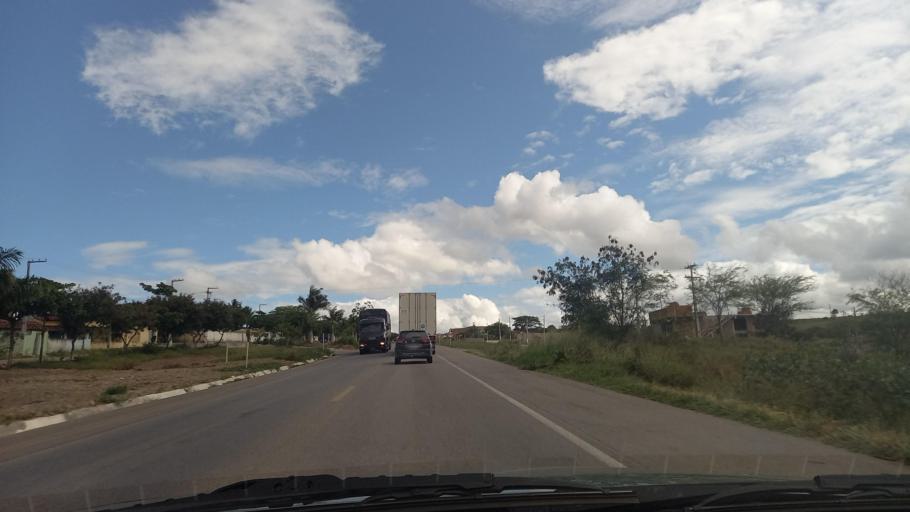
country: BR
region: Pernambuco
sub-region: Lajedo
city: Lajedo
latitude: -8.7048
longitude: -36.4171
